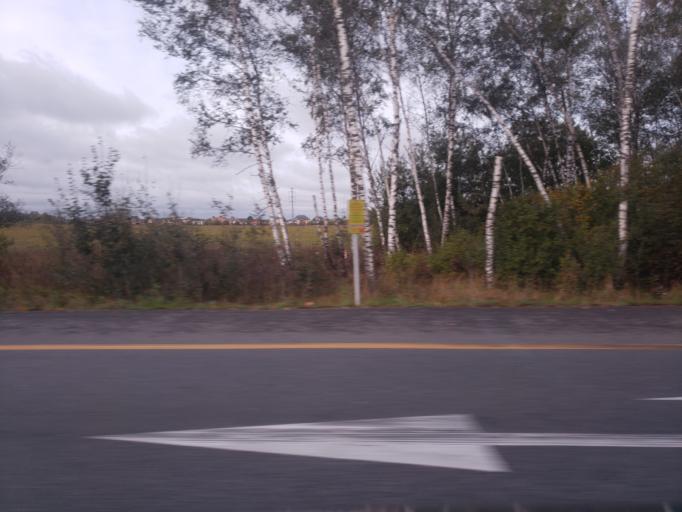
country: RU
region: Moskovskaya
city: Gorki-Leninskiye
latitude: 55.4840
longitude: 37.8508
